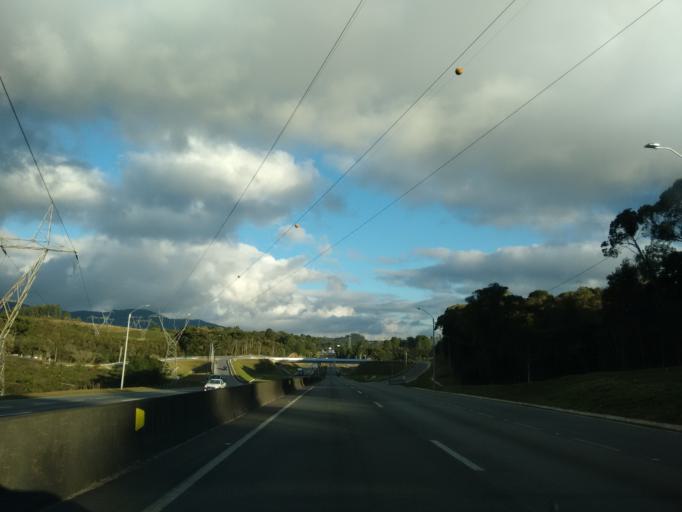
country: BR
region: Parana
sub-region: Sao Jose Dos Pinhais
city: Sao Jose dos Pinhais
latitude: -25.7260
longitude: -49.1351
